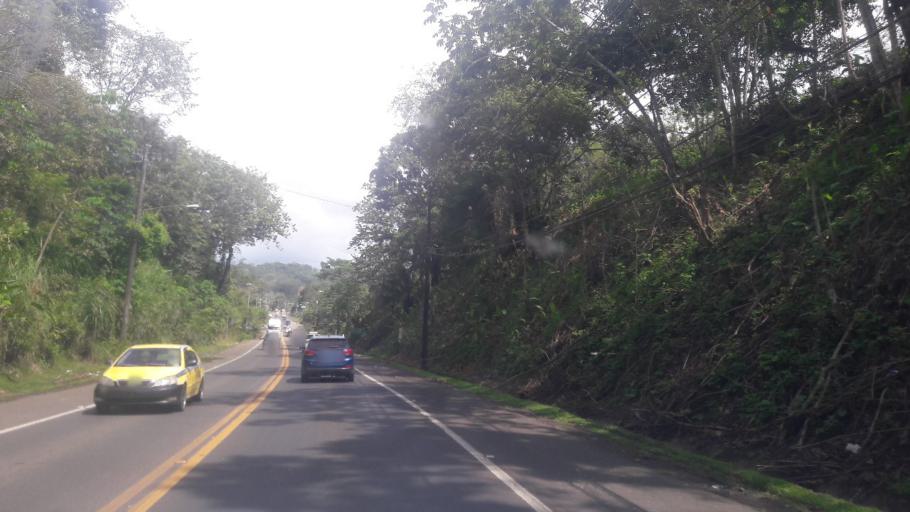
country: PA
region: Panama
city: Alcalde Diaz
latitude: 9.1237
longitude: -79.5904
